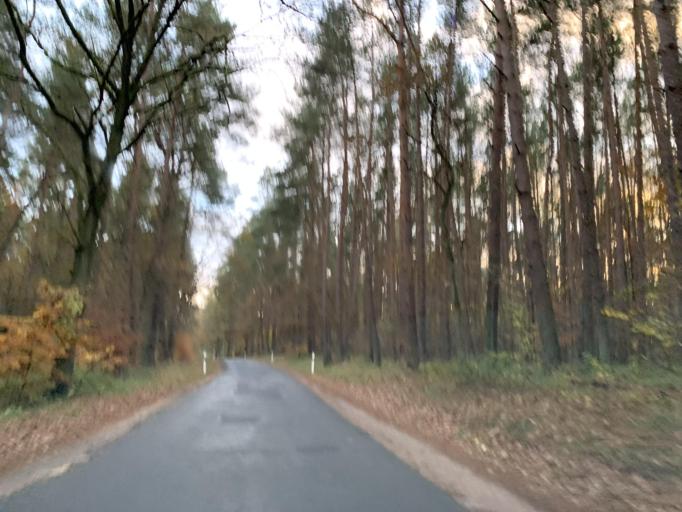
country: DE
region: Mecklenburg-Vorpommern
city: Blankensee
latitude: 53.3968
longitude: 13.2617
